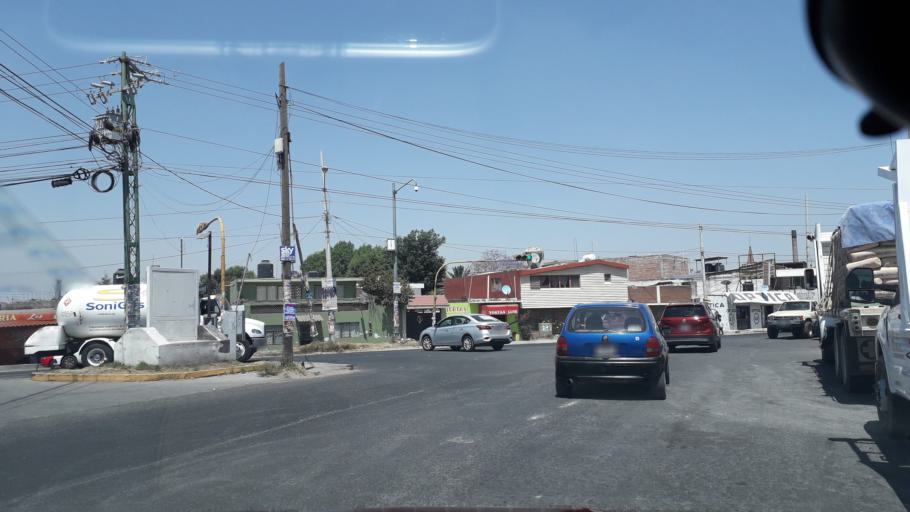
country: MX
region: Puebla
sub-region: Cuautlancingo
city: Sanctorum
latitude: 19.1007
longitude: -98.2284
